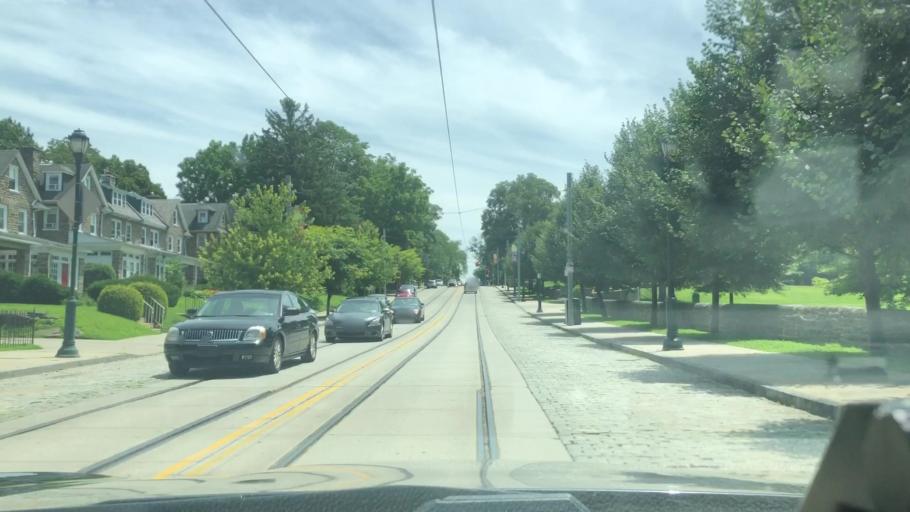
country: US
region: Pennsylvania
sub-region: Montgomery County
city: Wyndmoor
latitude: 40.0643
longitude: -75.1942
